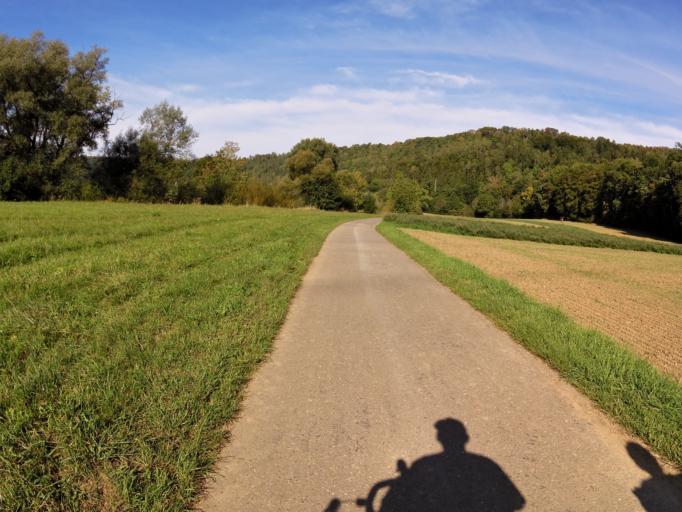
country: DE
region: Baden-Wuerttemberg
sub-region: Tuebingen Region
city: Hirrlingen
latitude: 48.4604
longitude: 8.8866
